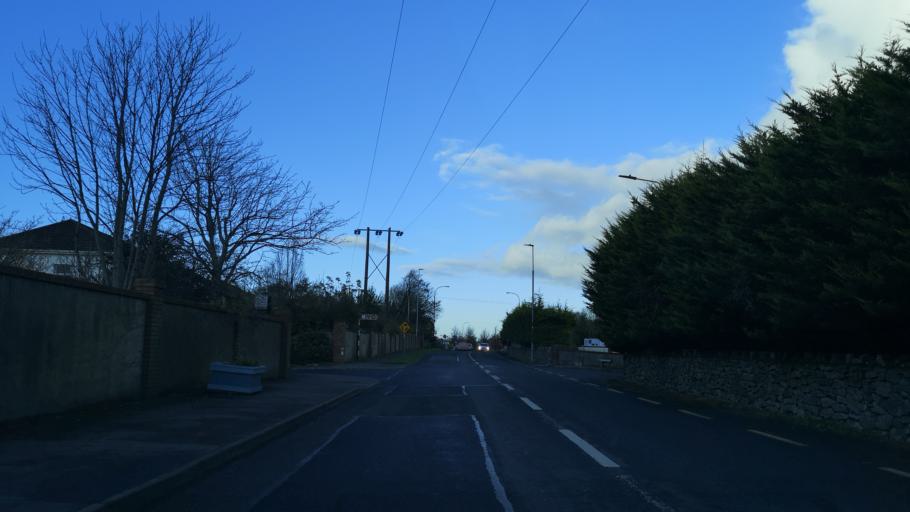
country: IE
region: Connaught
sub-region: County Galway
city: Oranmore
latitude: 53.2752
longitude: -8.9275
